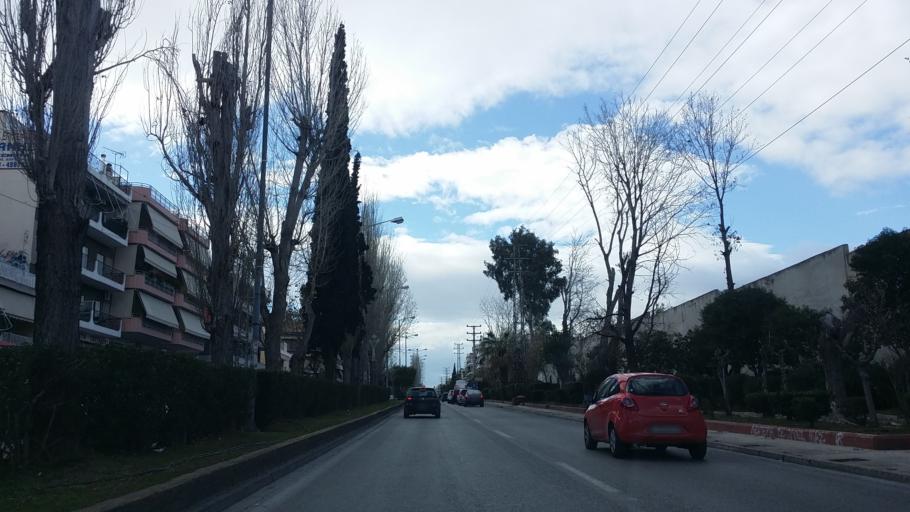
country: GR
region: Attica
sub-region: Nomos Piraios
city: Korydallos
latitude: 37.9810
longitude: 23.6509
